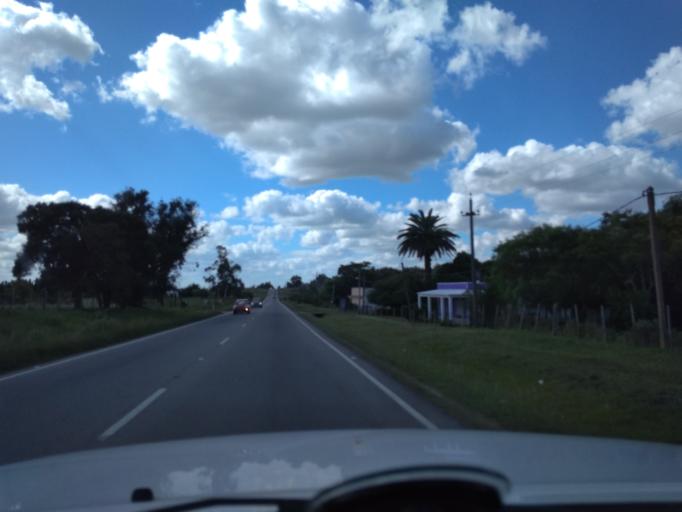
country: UY
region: Canelones
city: Joaquin Suarez
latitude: -34.7078
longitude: -56.0587
